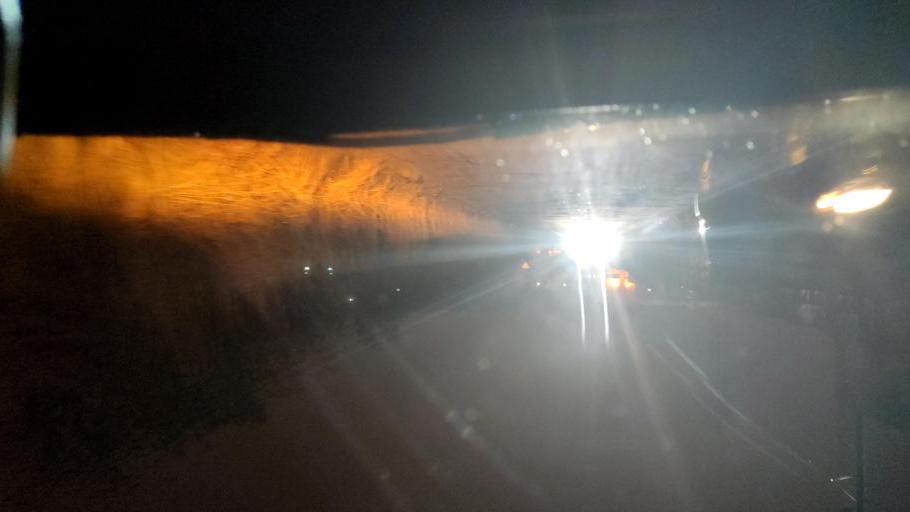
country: RU
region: Voronezj
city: Pridonskoy
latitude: 51.6382
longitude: 39.1102
